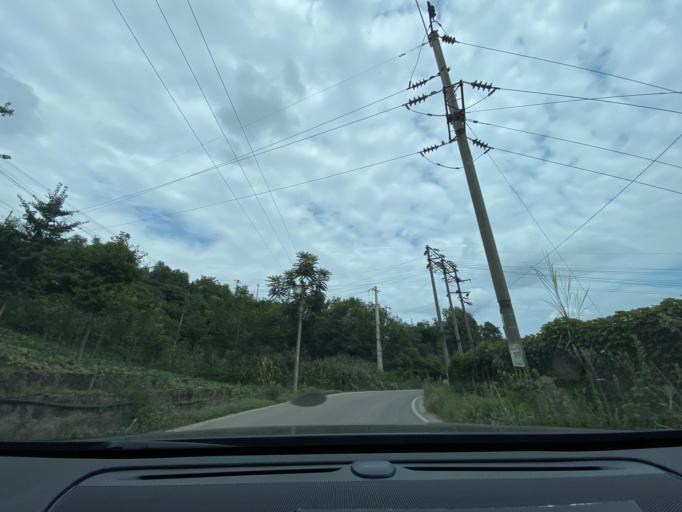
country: CN
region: Sichuan
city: Jiancheng
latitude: 30.4391
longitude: 104.5364
